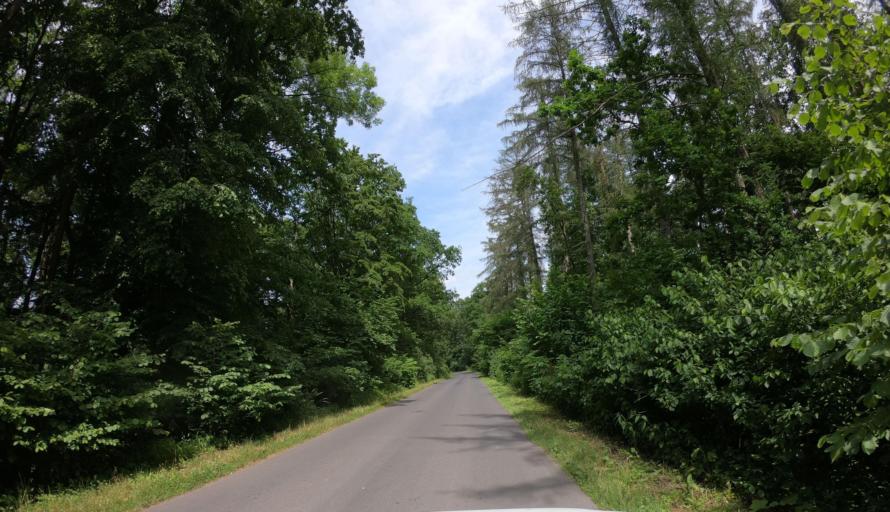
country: PL
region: West Pomeranian Voivodeship
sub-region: Powiat pyrzycki
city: Kozielice
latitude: 53.0773
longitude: 14.8261
